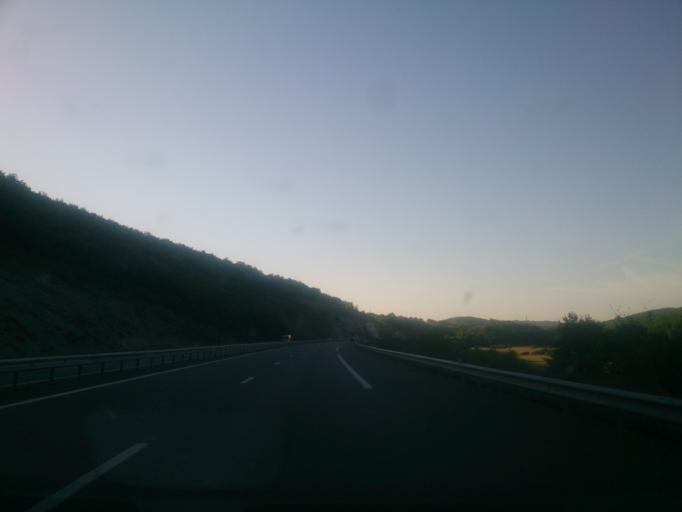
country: FR
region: Midi-Pyrenees
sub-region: Departement du Lot
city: Le Vigan
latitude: 44.7980
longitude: 1.5113
